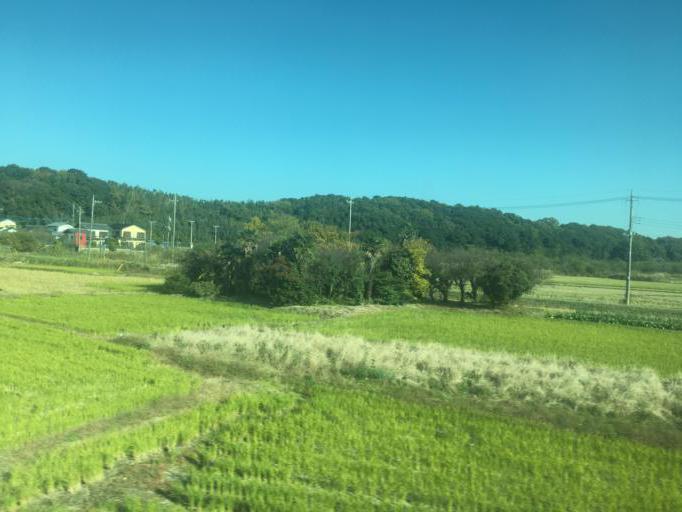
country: JP
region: Ibaraki
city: Ushiku
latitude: 35.9388
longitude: 140.1382
